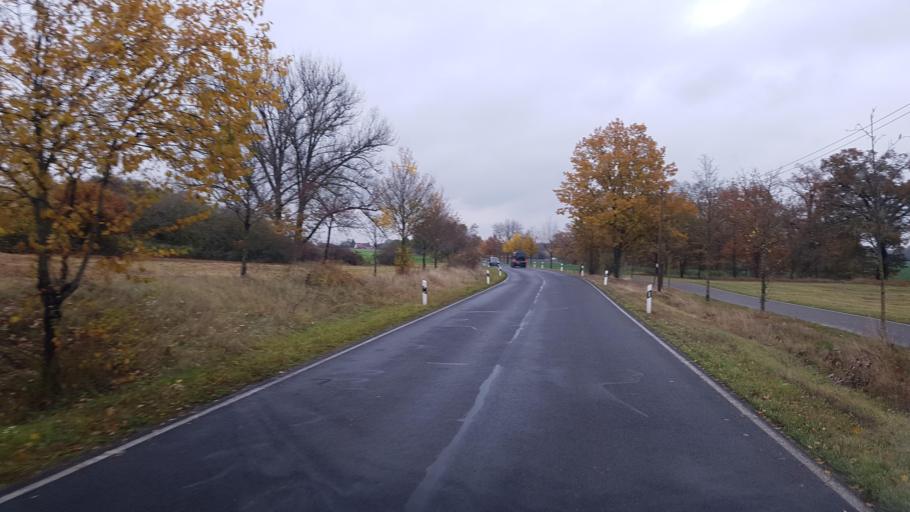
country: DE
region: Brandenburg
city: Drebkau
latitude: 51.6983
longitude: 14.2283
